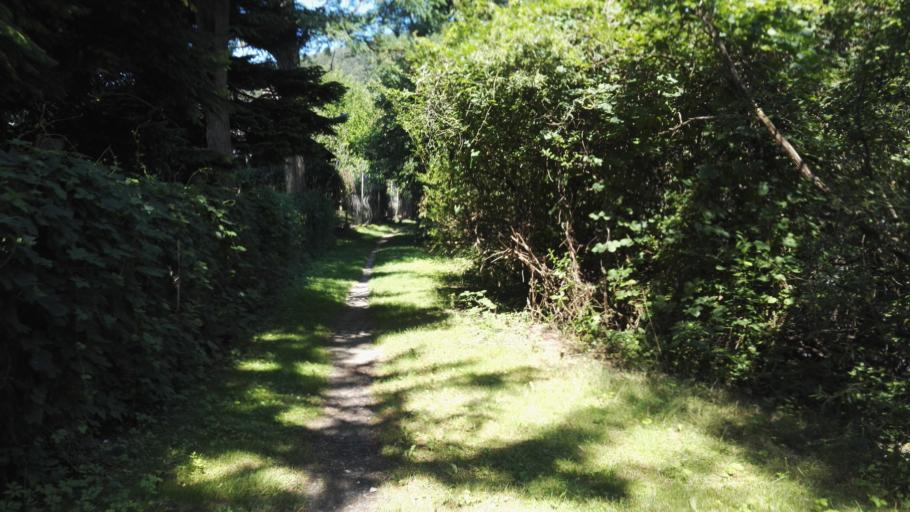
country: AT
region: Styria
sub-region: Politischer Bezirk Graz-Umgebung
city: Peggau
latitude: 47.2028
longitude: 15.3391
